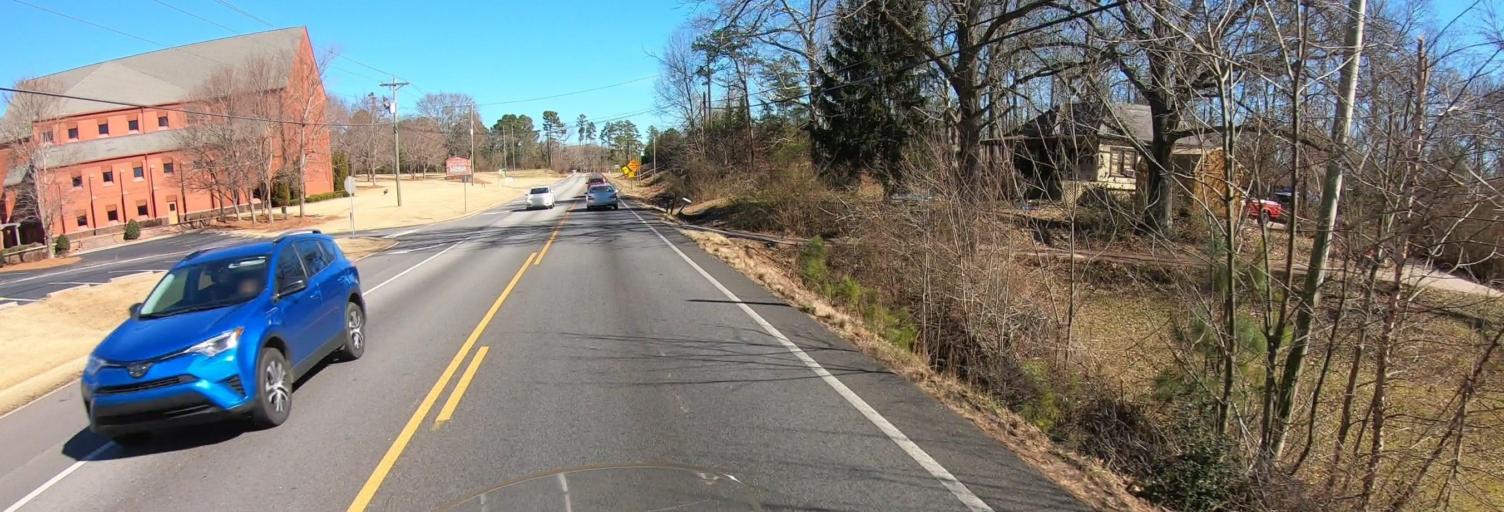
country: US
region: Georgia
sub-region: Hall County
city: Oakwood
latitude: 34.2792
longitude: -83.9007
